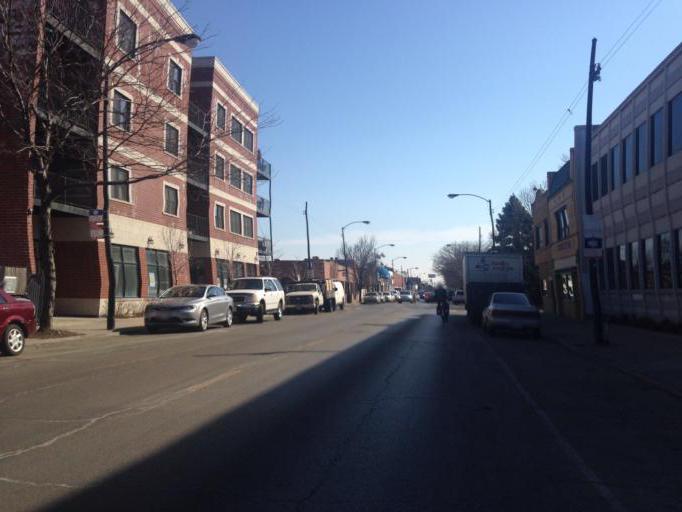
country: US
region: Illinois
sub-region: Cook County
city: Lincolnwood
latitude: 41.9490
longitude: -87.7079
